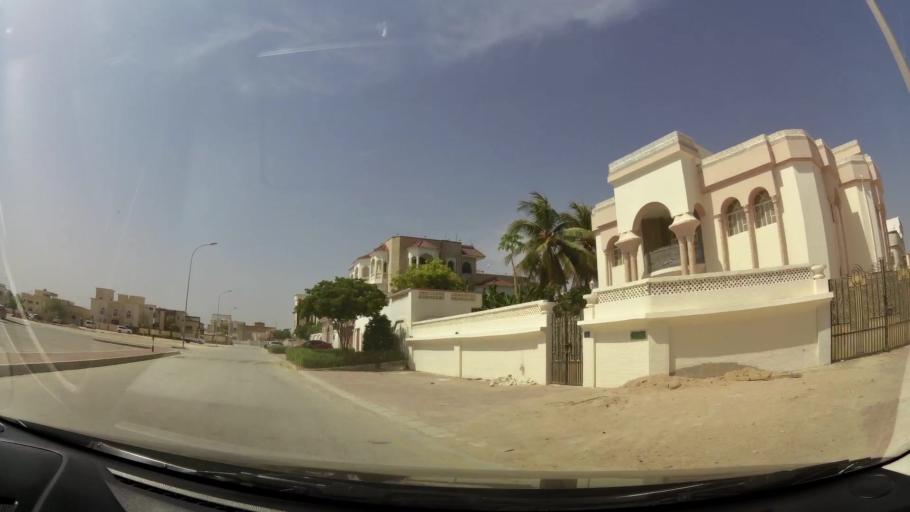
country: OM
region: Zufar
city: Salalah
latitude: 17.0402
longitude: 54.1529
